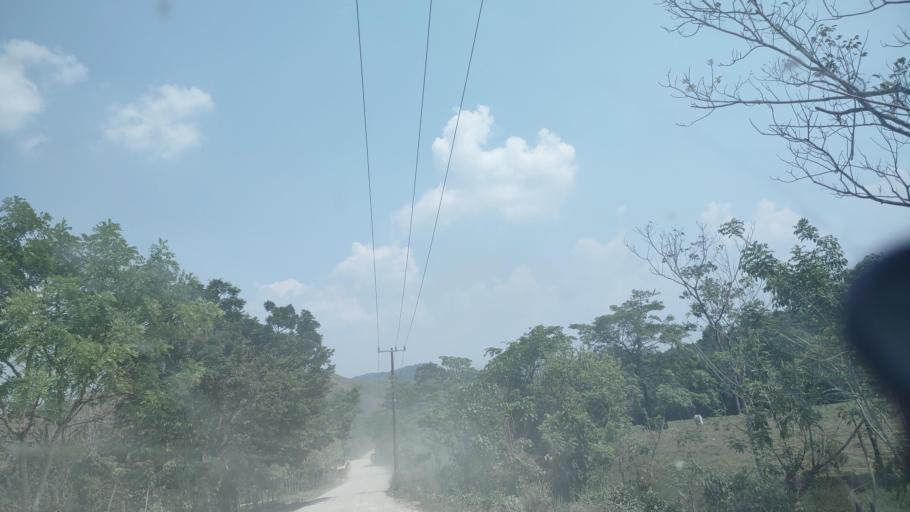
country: MX
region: Tabasco
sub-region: Huimanguillo
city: Francisco Rueda
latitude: 17.5816
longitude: -93.8911
